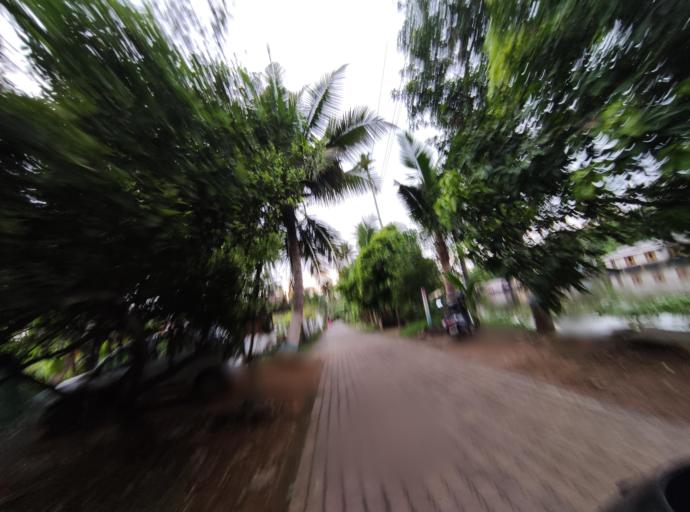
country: IN
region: Kerala
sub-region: Alappuzha
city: Shertallai
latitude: 9.6309
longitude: 76.4264
